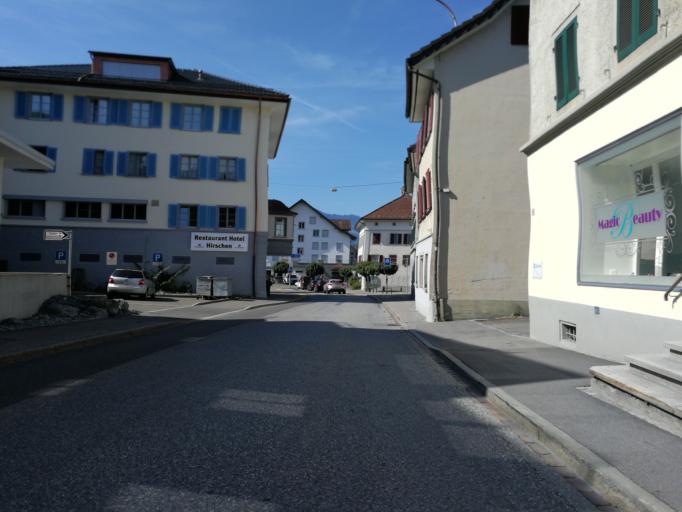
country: CH
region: Saint Gallen
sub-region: Wahlkreis See-Gaster
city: Kaltbrunn
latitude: 47.2140
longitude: 9.0258
